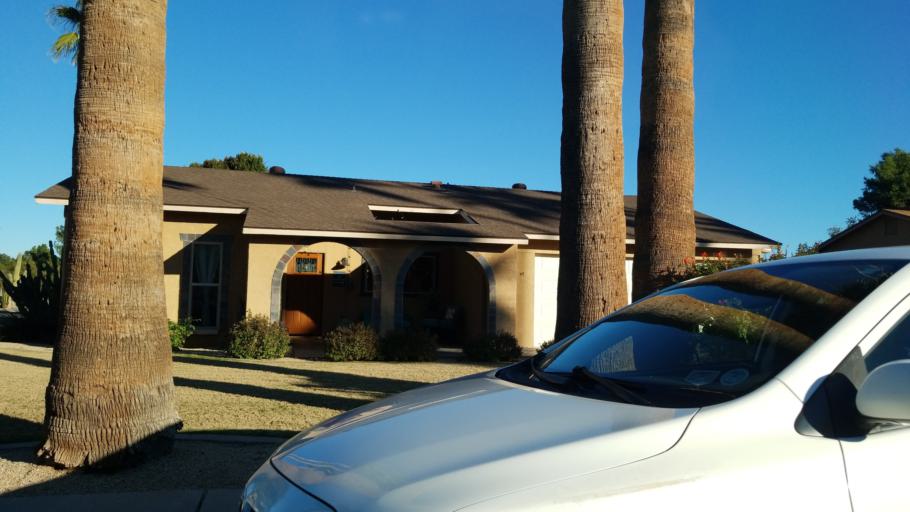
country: US
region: Arizona
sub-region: Maricopa County
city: Paradise Valley
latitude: 33.6033
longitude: -111.9730
